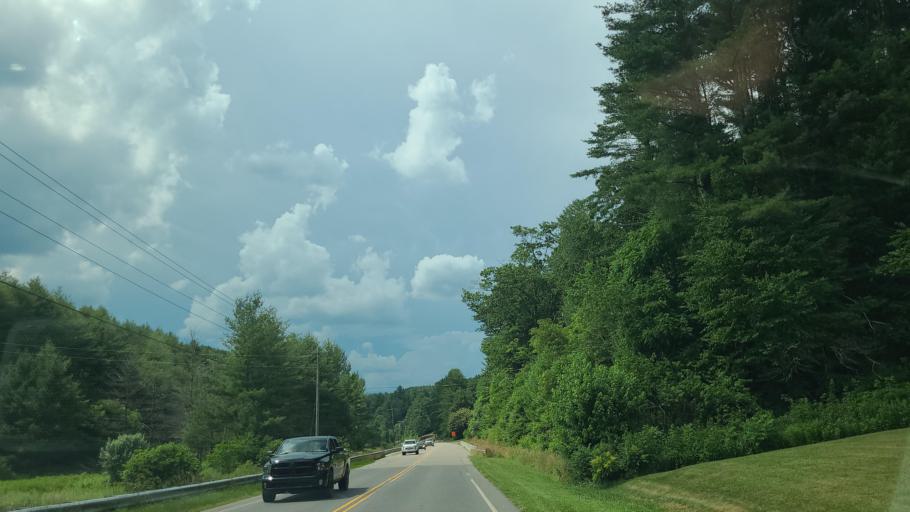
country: US
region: North Carolina
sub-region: Ashe County
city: Jefferson
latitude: 36.3646
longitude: -81.3901
